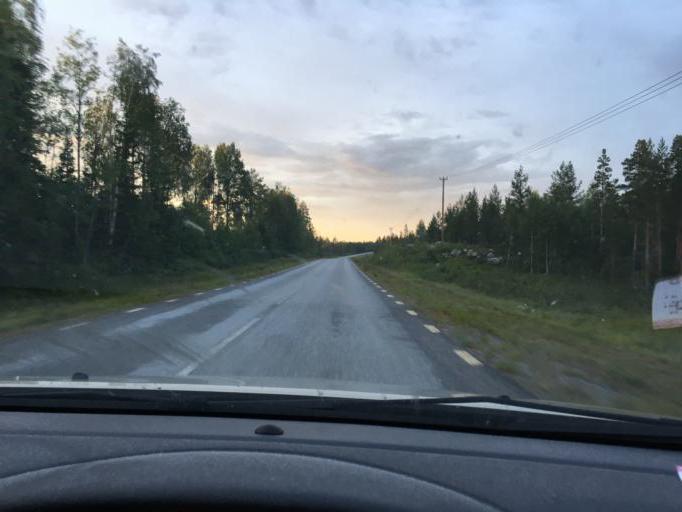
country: SE
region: Norrbotten
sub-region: Kalix Kommun
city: Toere
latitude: 66.0573
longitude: 22.5968
